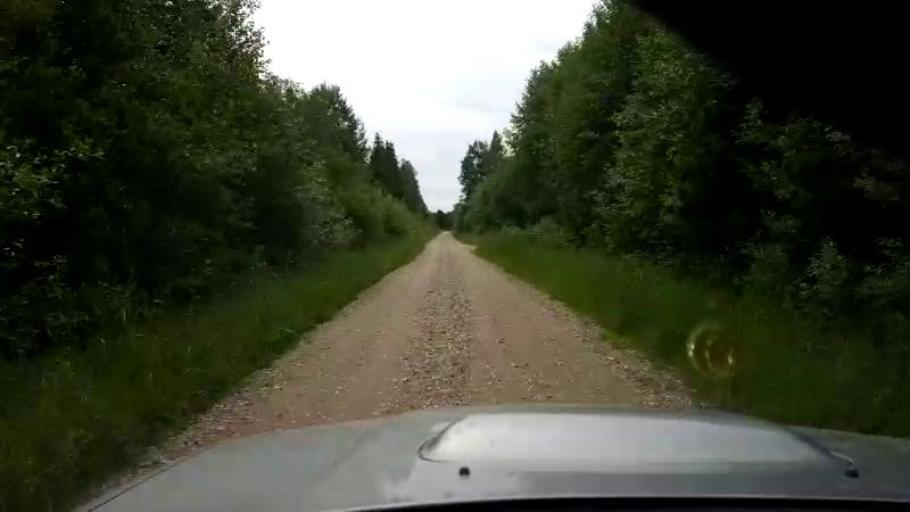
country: EE
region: Paernumaa
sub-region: Tootsi vald
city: Tootsi
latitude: 58.5534
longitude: 24.7468
